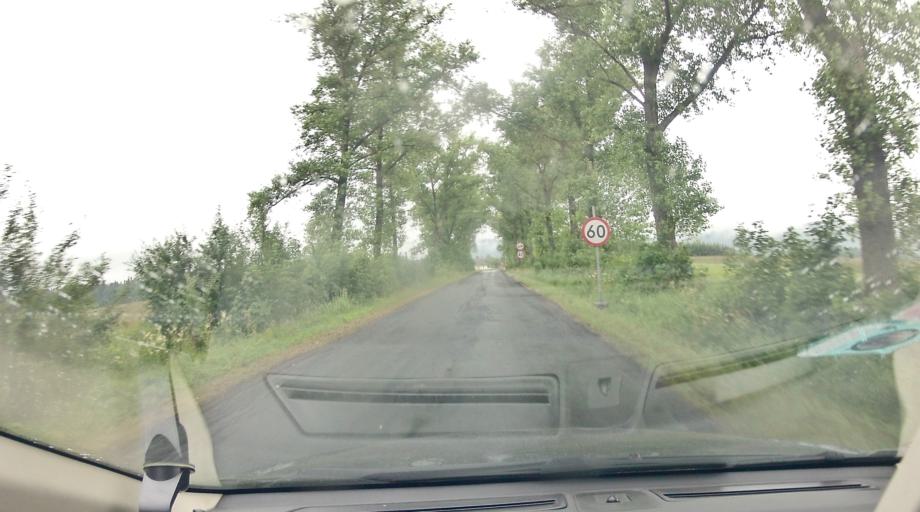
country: PL
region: Lower Silesian Voivodeship
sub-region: Powiat klodzki
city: Miedzylesie
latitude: 50.1580
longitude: 16.6878
